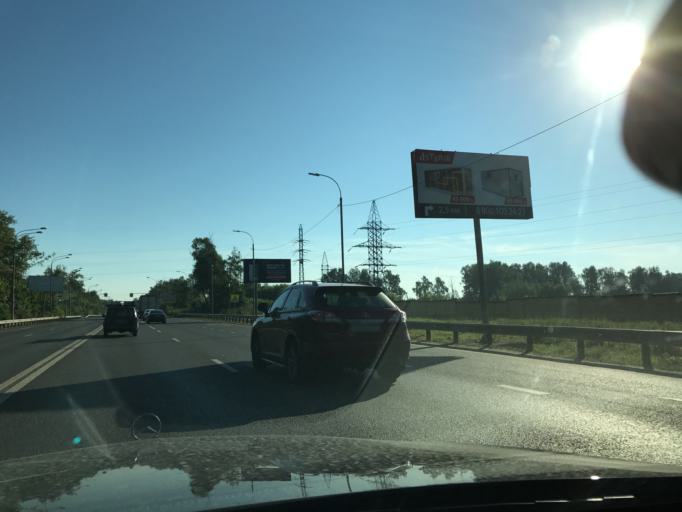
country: RU
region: Moskovskaya
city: Balashikha
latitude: 55.8454
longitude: 37.9583
